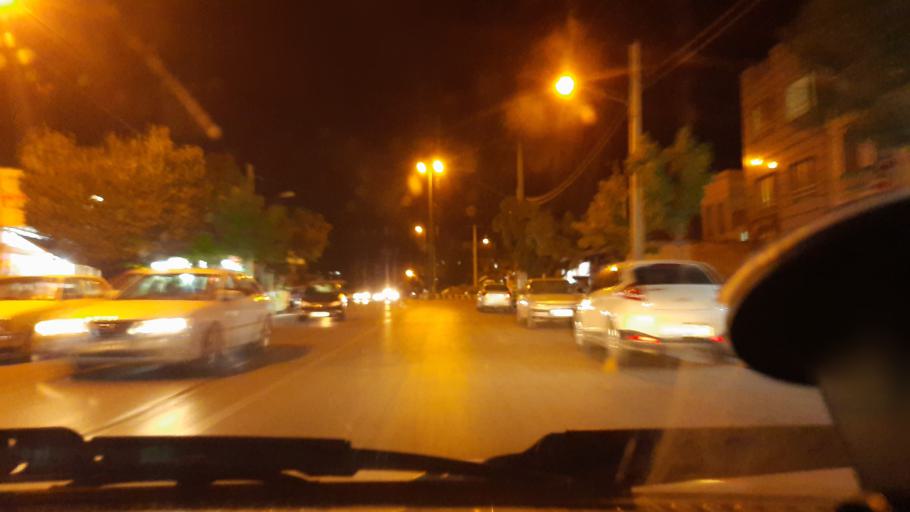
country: IR
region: Markazi
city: Arak
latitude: 34.0736
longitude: 49.6812
